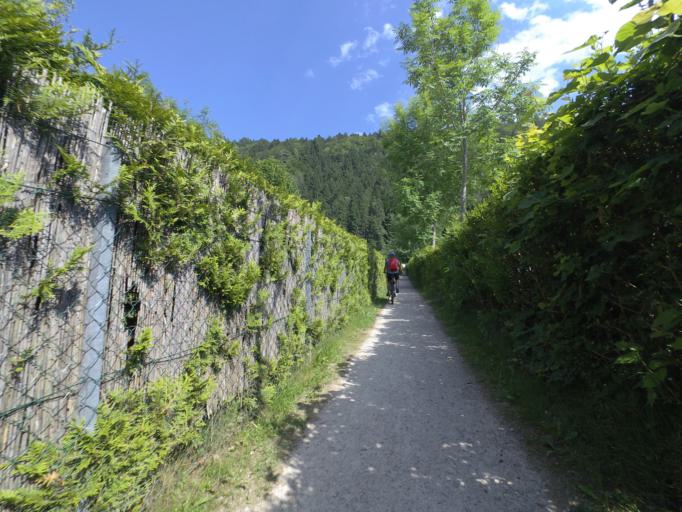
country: AT
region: Carinthia
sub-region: Politischer Bezirk Villach Land
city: Ferndorf
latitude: 46.7687
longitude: 13.6478
